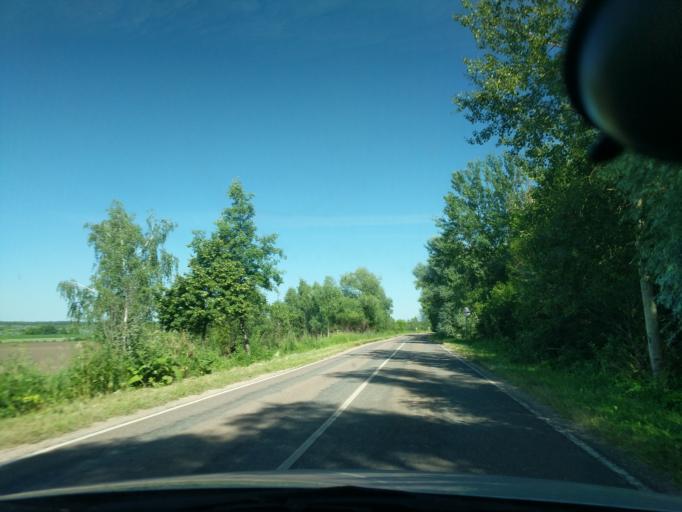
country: RU
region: Moskovskaya
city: Pushchino
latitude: 54.8418
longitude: 37.5545
